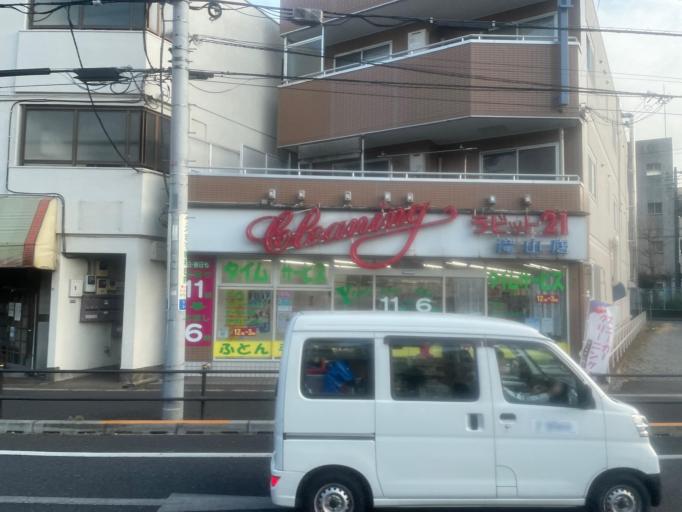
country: JP
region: Tokyo
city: Higashimurayama-shi
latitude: 35.7522
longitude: 139.4981
